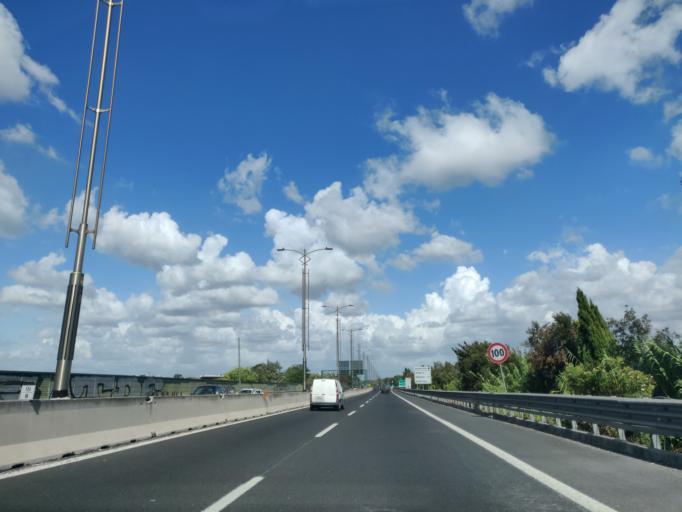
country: IT
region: Latium
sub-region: Citta metropolitana di Roma Capitale
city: Vitinia
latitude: 41.8189
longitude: 12.3976
